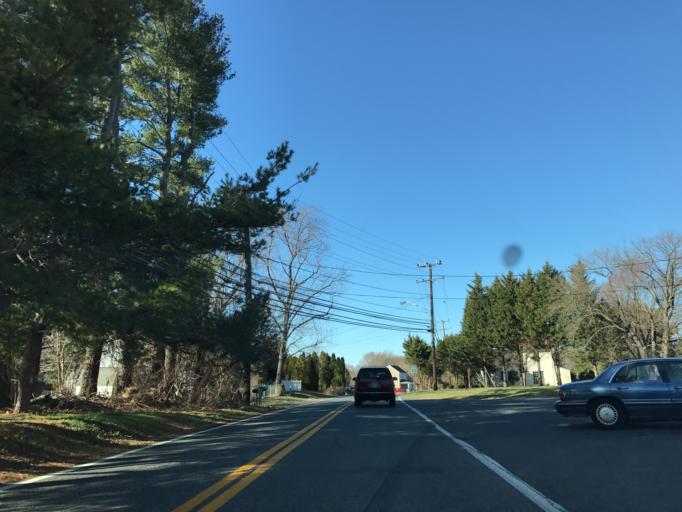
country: US
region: Maryland
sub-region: Harford County
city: Perryman
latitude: 39.4684
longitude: -76.2042
